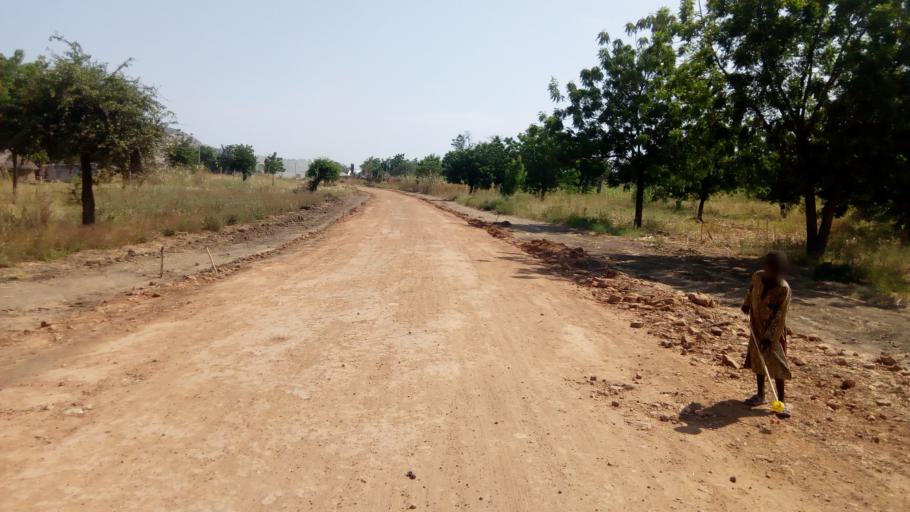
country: NG
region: Adamawa
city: Numan
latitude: 9.6842
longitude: 11.8694
